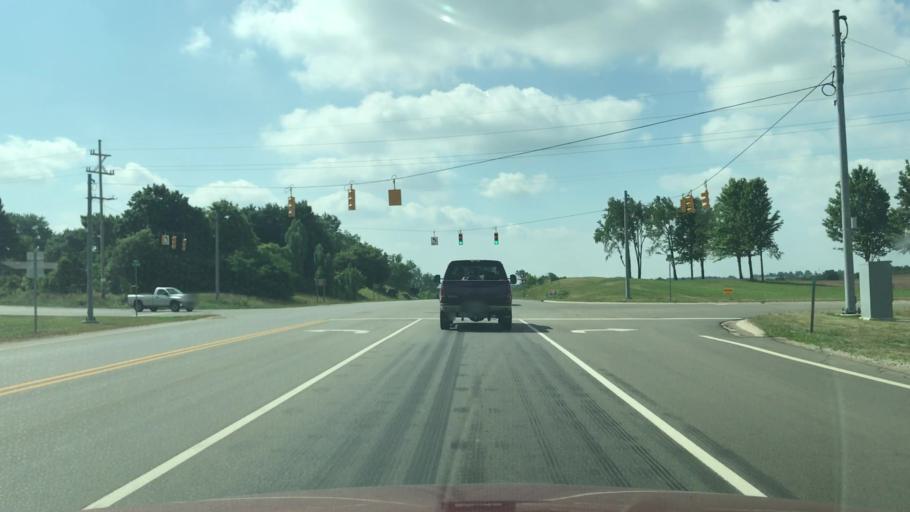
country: US
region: Michigan
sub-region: Kent County
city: Sparta
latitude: 43.1469
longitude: -85.7221
